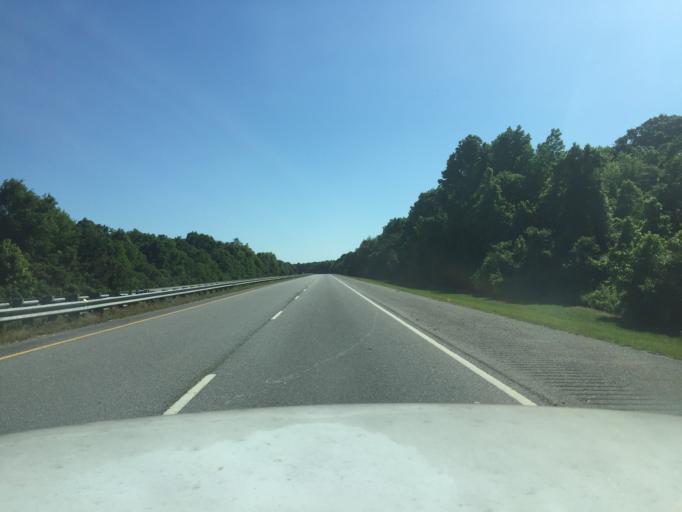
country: US
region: Georgia
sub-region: Chatham County
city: Georgetown
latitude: 32.0114
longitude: -81.1834
